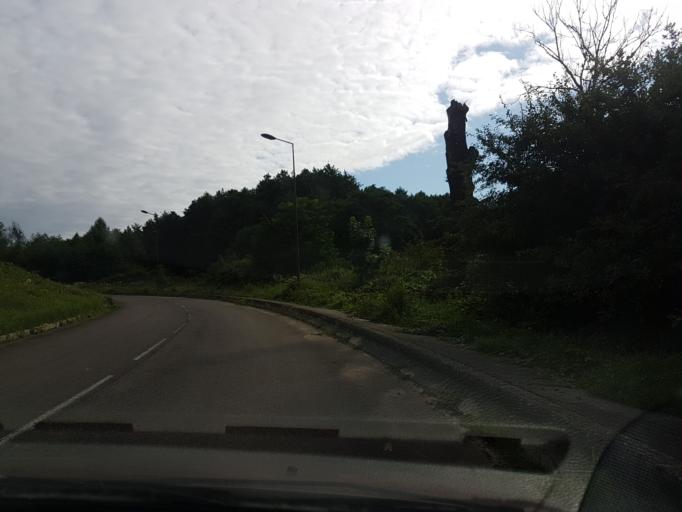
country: FR
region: Franche-Comte
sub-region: Departement de la Haute-Saone
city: Luxeuil-les-Bains
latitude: 47.8085
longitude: 6.3651
